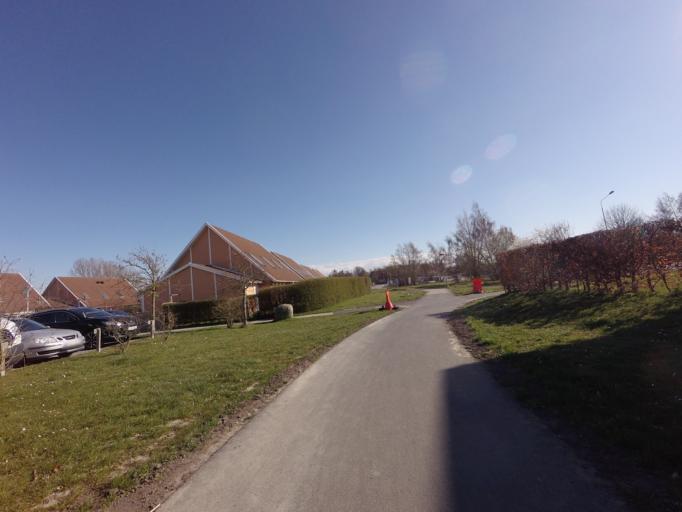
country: SE
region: Skane
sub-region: Staffanstorps Kommun
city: Hjaerup
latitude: 55.6575
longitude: 13.1039
